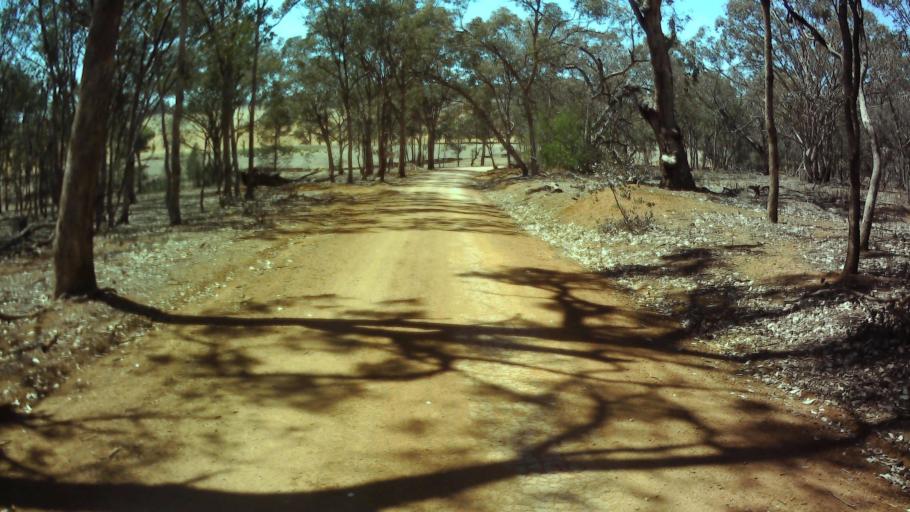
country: AU
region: New South Wales
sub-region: Weddin
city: Grenfell
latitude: -33.9475
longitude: 148.0830
